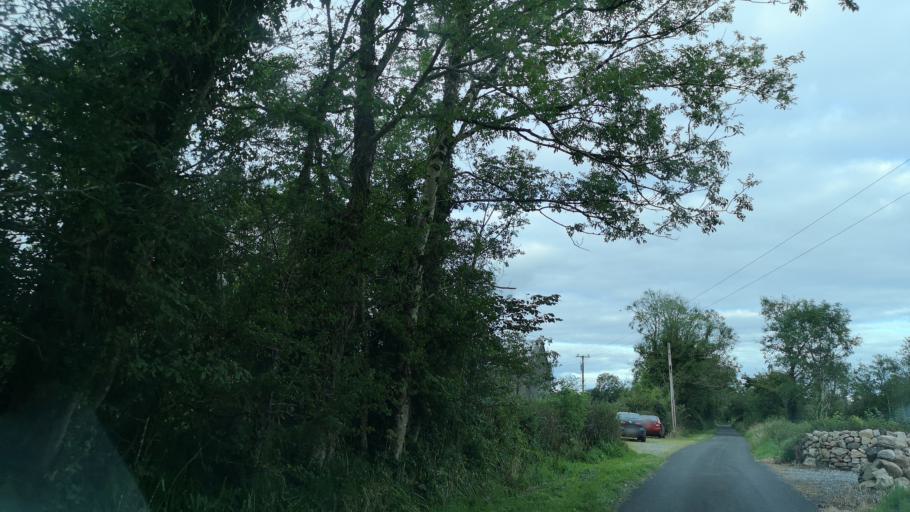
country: IE
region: Connaught
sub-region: County Galway
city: Loughrea
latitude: 53.1488
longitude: -8.5079
